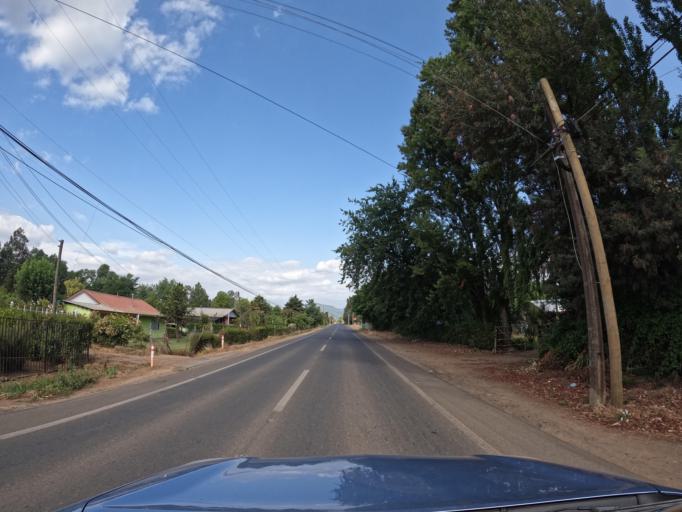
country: CL
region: Maule
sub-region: Provincia de Curico
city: Molina
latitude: -35.2767
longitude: -71.2841
